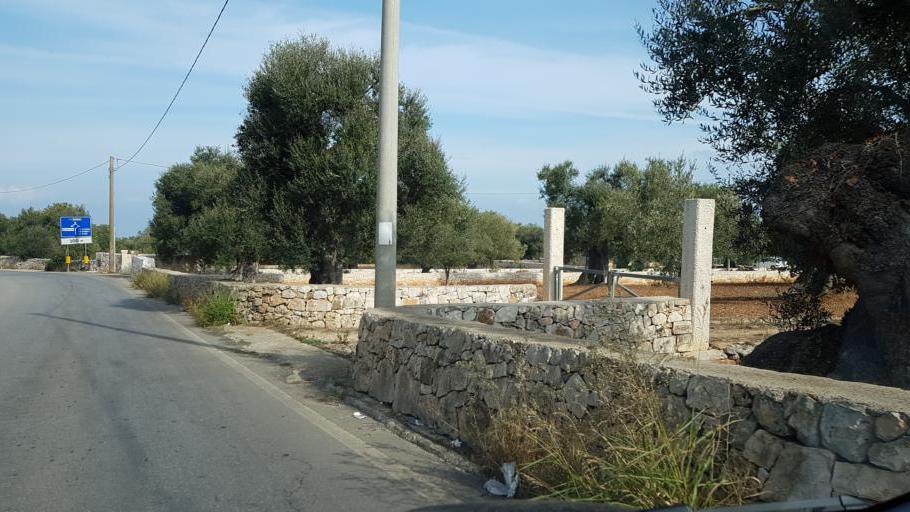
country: IT
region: Apulia
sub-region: Provincia di Brindisi
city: Ostuni
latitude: 40.7379
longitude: 17.5795
